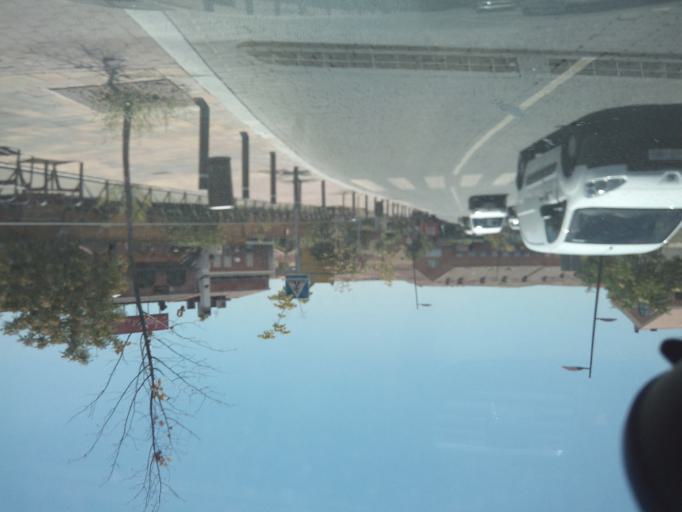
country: ES
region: Madrid
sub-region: Provincia de Madrid
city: Cobena
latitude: 40.5684
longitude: -3.5031
